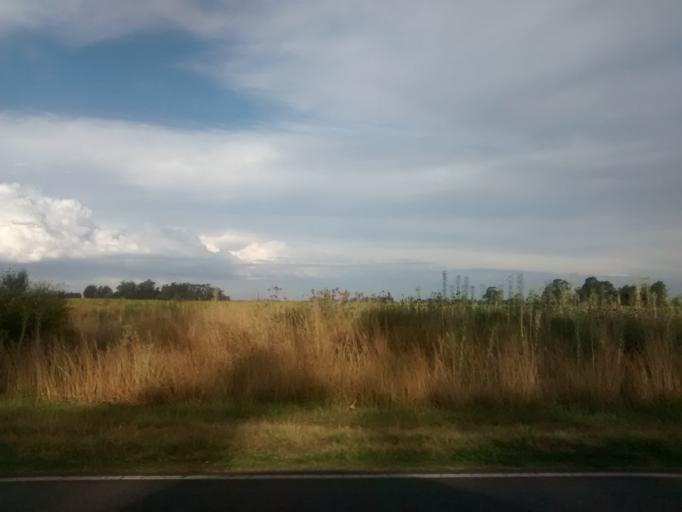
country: AR
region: Buenos Aires
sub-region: Partido de Loberia
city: Loberia
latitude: -38.2117
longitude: -58.7332
